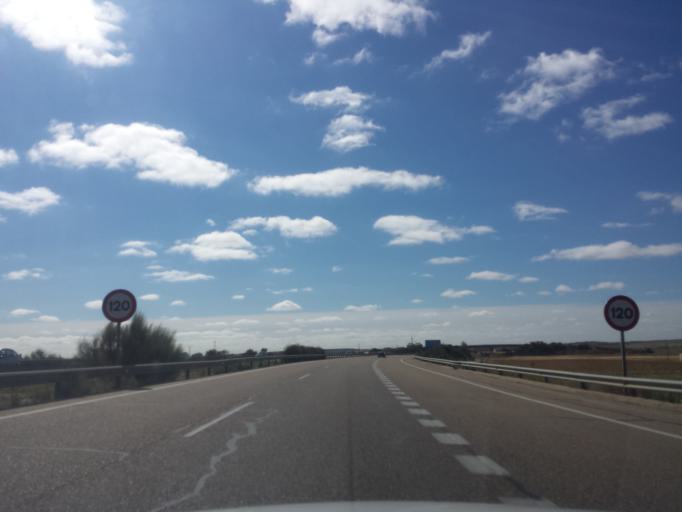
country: ES
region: Castille and Leon
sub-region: Provincia de Zamora
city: Villalpando
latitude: 41.8680
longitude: -5.4327
